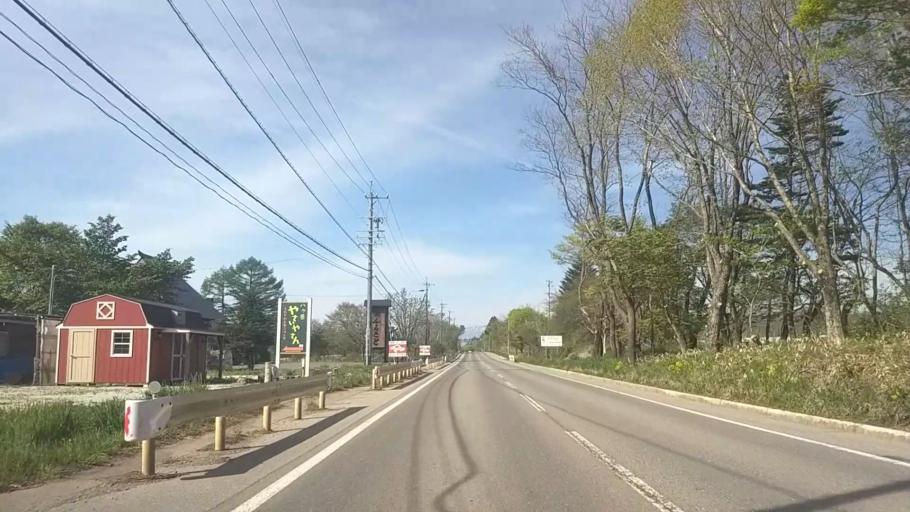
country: JP
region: Yamanashi
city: Nirasaki
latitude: 35.9532
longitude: 138.4608
